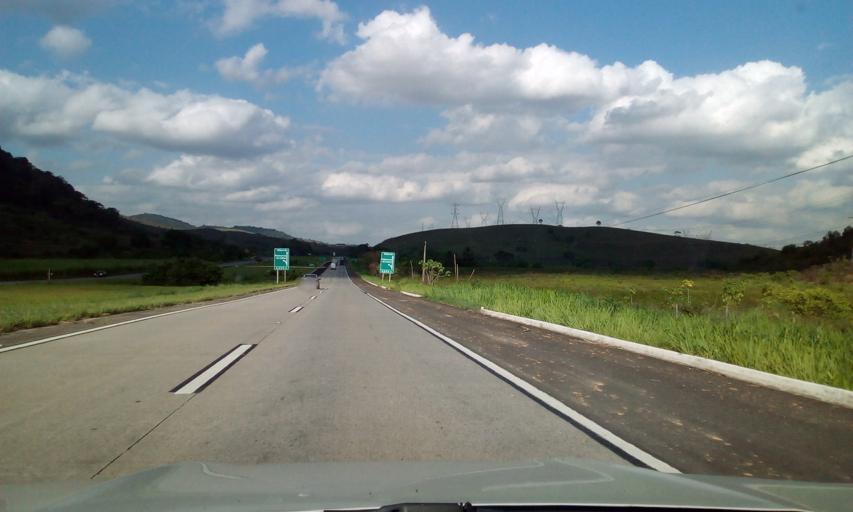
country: BR
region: Pernambuco
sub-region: Joaquim Nabuco
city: Joaquim Nabuco
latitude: -8.6015
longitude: -35.5313
